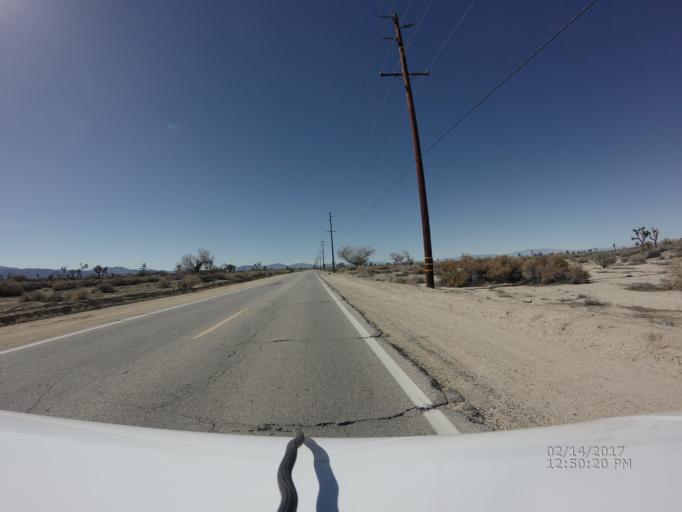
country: US
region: California
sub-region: Los Angeles County
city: Lake Los Angeles
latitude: 34.5801
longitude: -117.8834
